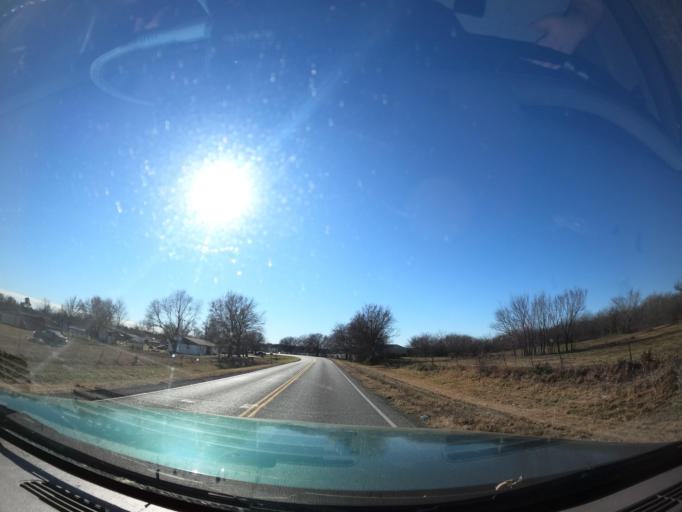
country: US
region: Oklahoma
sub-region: Muskogee County
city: Haskell
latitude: 35.6557
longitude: -95.6541
